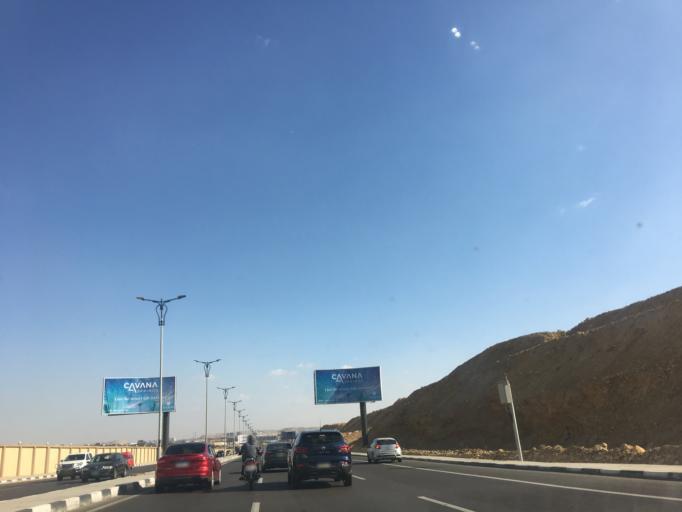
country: EG
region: Muhafazat al Qahirah
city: Cairo
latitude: 30.0276
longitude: 31.3145
